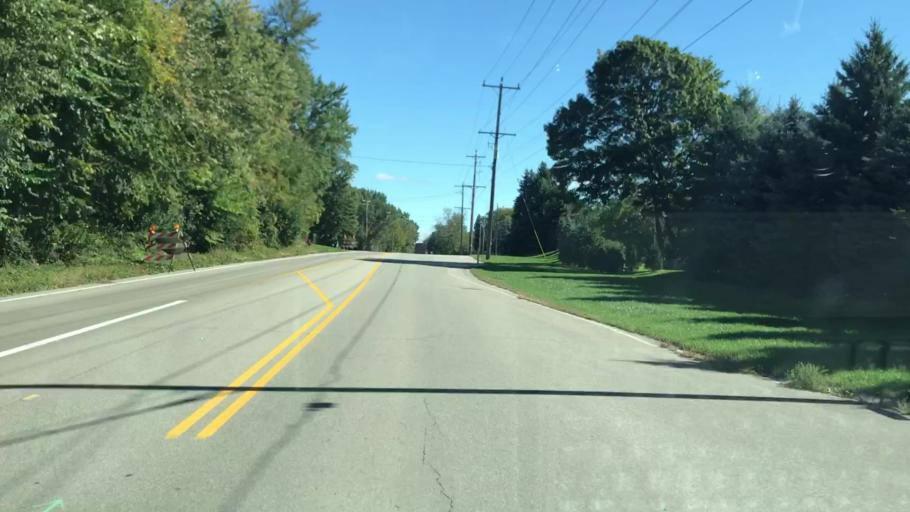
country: US
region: Wisconsin
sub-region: Waukesha County
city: Lannon
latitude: 43.1046
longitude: -88.1375
